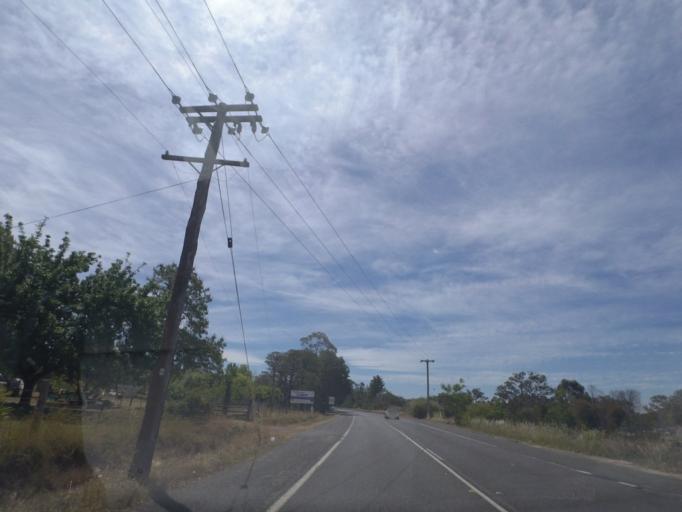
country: AU
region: New South Wales
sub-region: Wollondilly
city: Buxton
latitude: -34.2724
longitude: 150.5755
